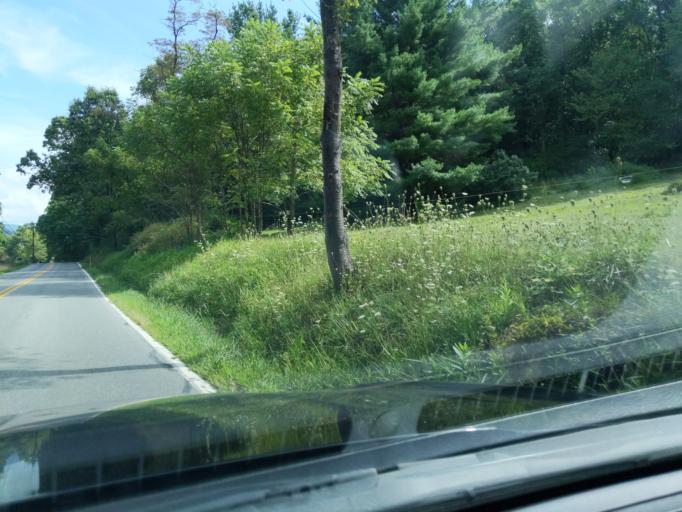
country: US
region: Pennsylvania
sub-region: Blair County
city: Hollidaysburg
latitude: 40.3951
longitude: -78.3982
